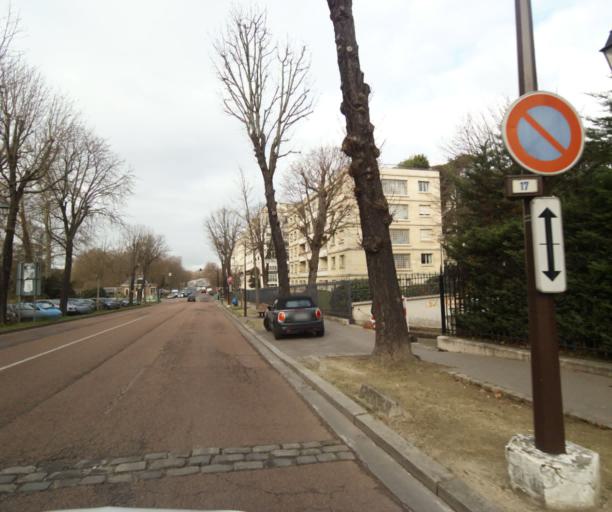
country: FR
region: Ile-de-France
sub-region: Departement des Hauts-de-Seine
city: Puteaux
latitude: 48.8752
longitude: 2.2510
